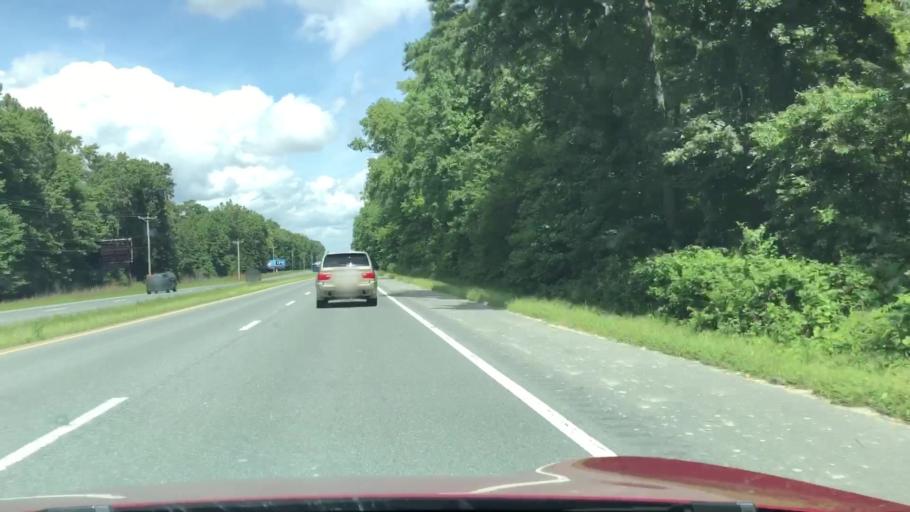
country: US
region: Virginia
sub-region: Northampton County
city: Cape Charles
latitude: 37.1953
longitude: -75.9673
